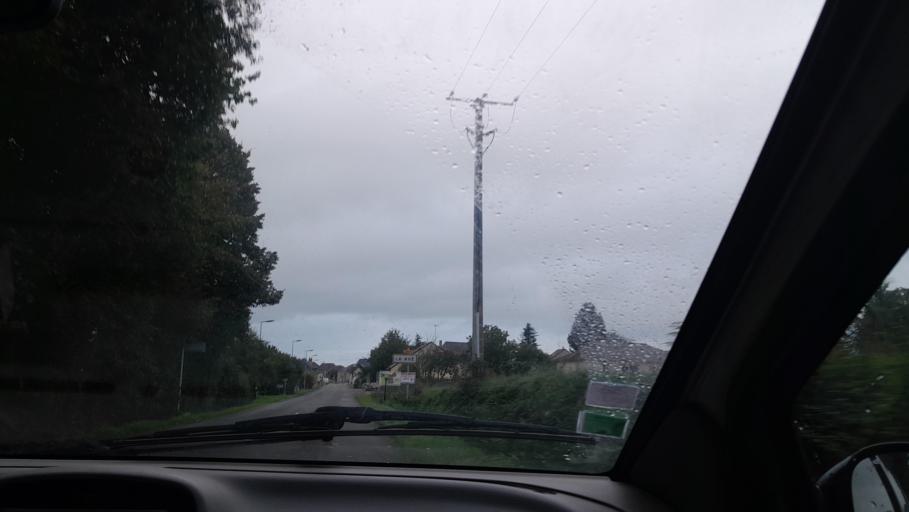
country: FR
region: Pays de la Loire
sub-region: Departement de la Mayenne
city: Ballots
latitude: 47.8930
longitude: -1.1143
